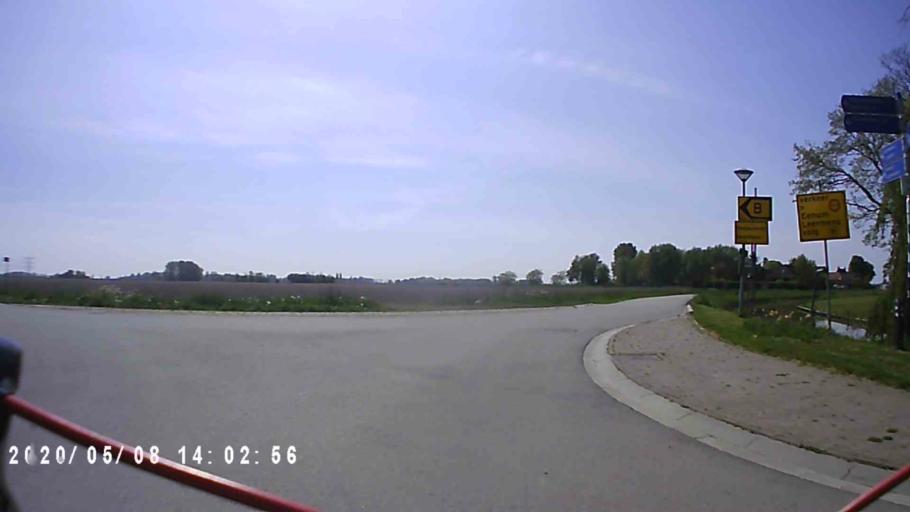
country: NL
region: Groningen
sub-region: Gemeente Appingedam
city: Appingedam
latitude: 53.3376
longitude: 6.8124
